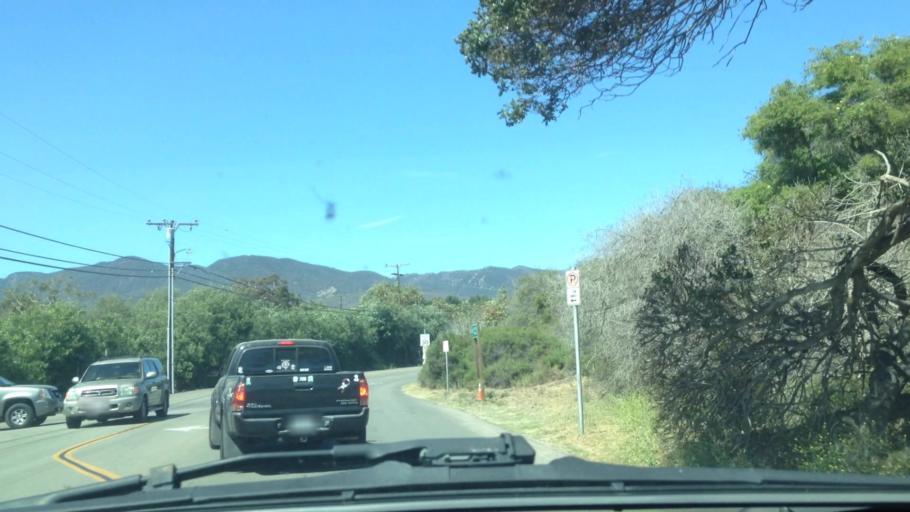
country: US
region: California
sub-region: Los Angeles County
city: Malibu
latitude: 34.0149
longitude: -118.8187
